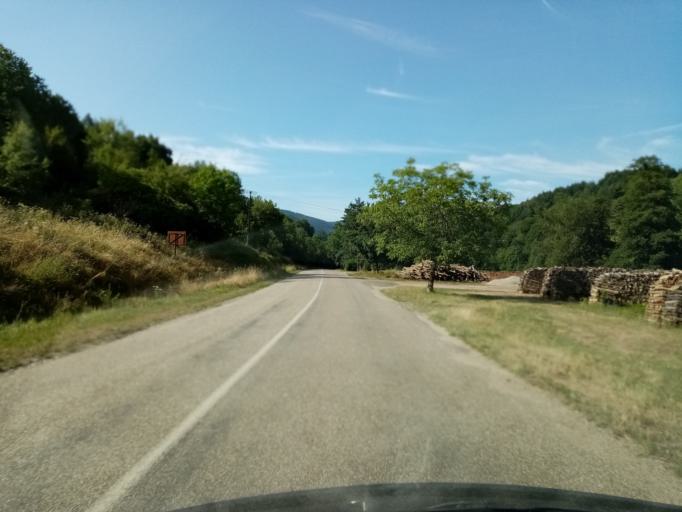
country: FR
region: Alsace
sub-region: Departement du Bas-Rhin
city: Ville
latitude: 48.3522
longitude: 7.3123
